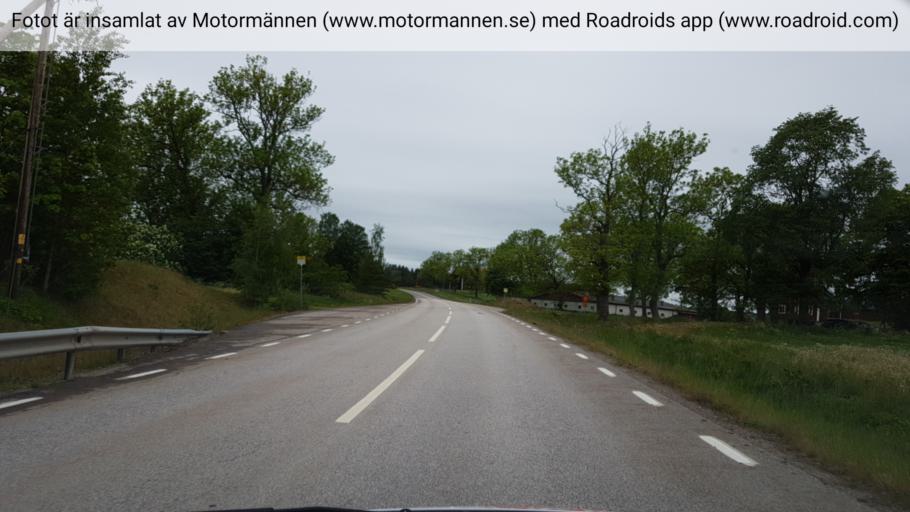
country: SE
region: Kalmar
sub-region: Vasterviks Kommun
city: Forserum
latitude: 57.9411
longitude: 16.4941
